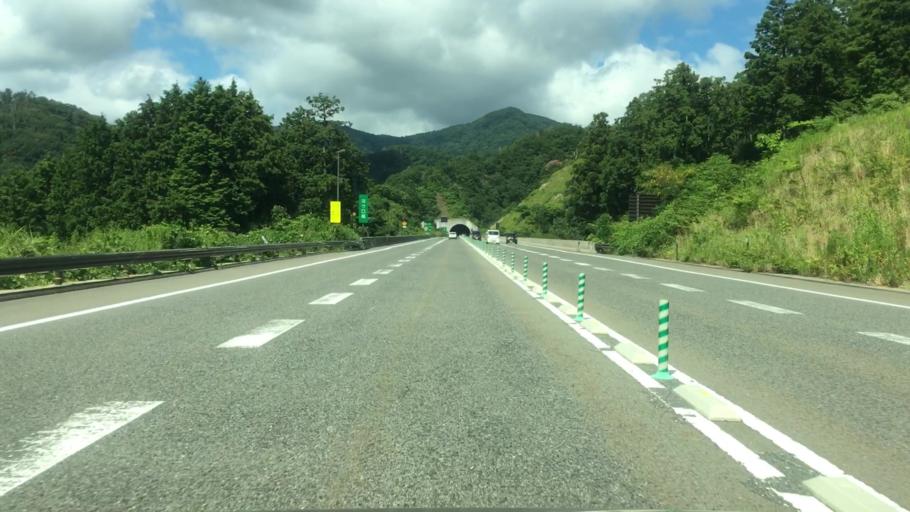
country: JP
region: Hyogo
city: Toyooka
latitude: 35.6291
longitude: 134.6167
